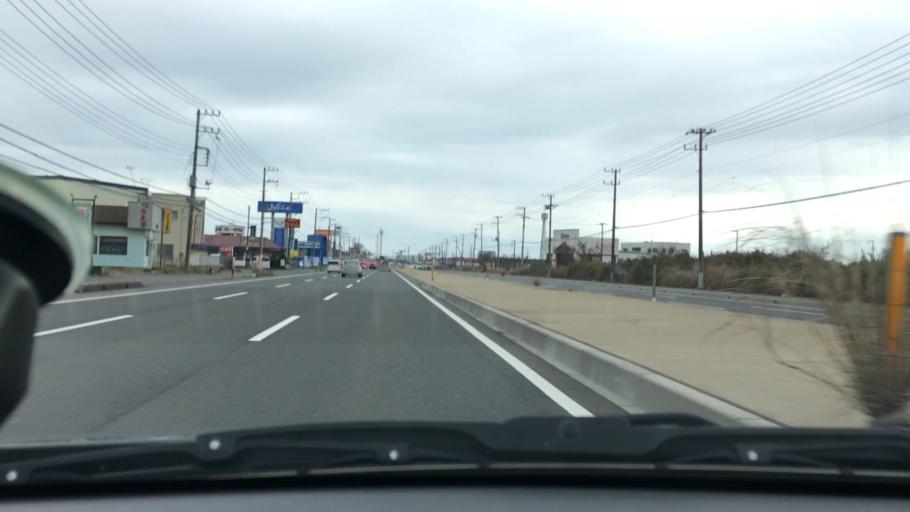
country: JP
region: Chiba
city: Omigawa
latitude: 35.8860
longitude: 140.6721
